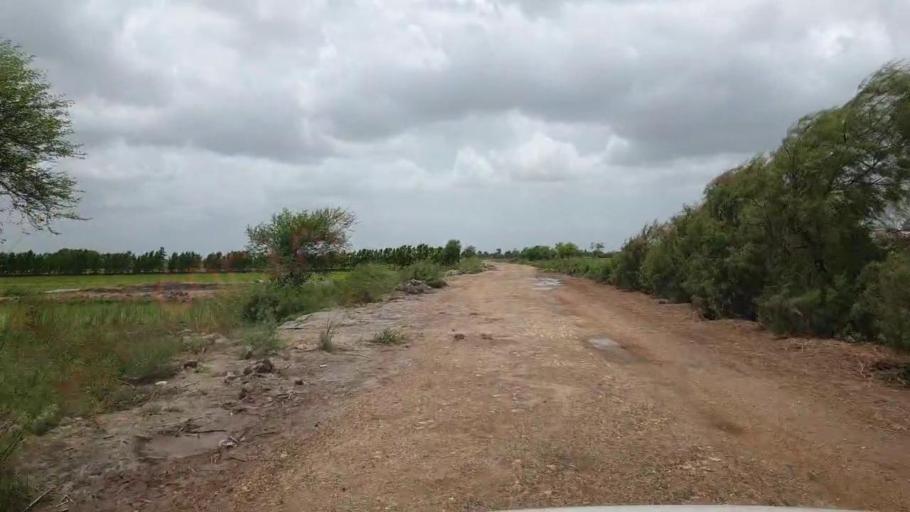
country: PK
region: Sindh
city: Kario
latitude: 24.7439
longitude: 68.5080
